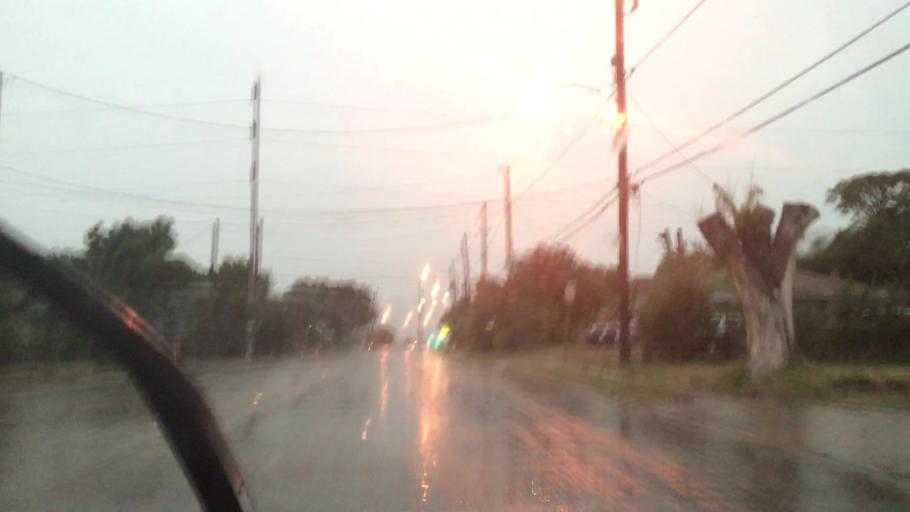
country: US
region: Texas
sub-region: Dallas County
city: Dallas
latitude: 32.8076
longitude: -96.8225
